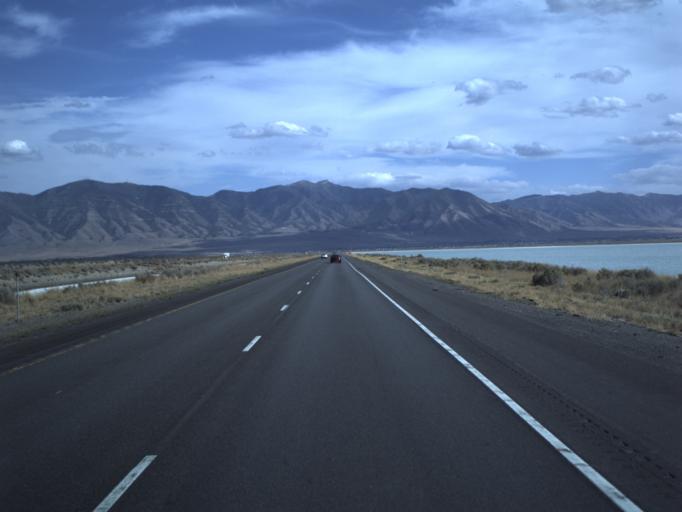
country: US
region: Utah
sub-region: Tooele County
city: Grantsville
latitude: 40.6751
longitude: -112.4018
